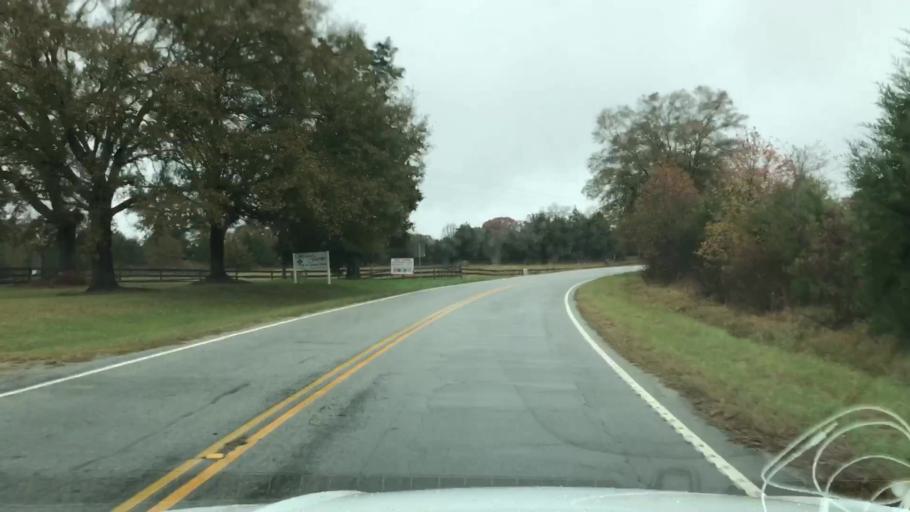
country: US
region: South Carolina
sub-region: Spartanburg County
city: Roebuck
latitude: 34.8173
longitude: -81.9269
